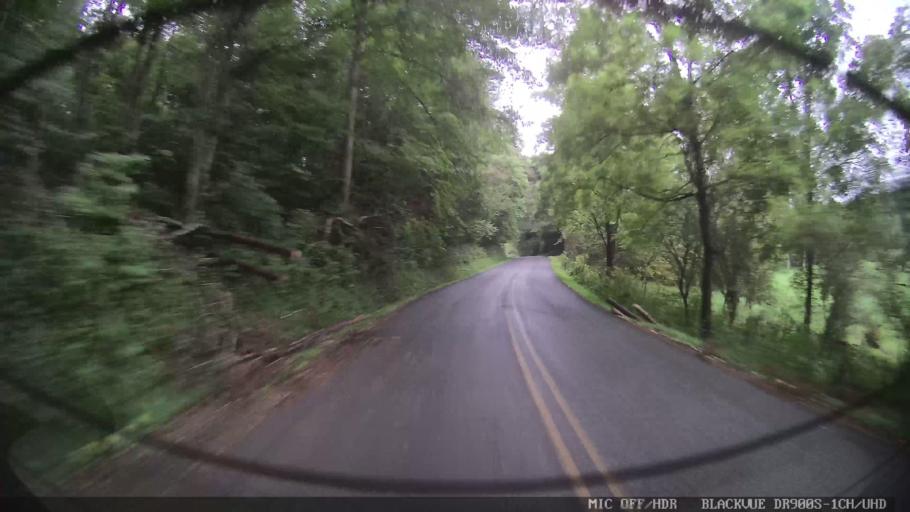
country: US
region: Georgia
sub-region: Gilmer County
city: Ellijay
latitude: 34.7651
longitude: -84.5316
